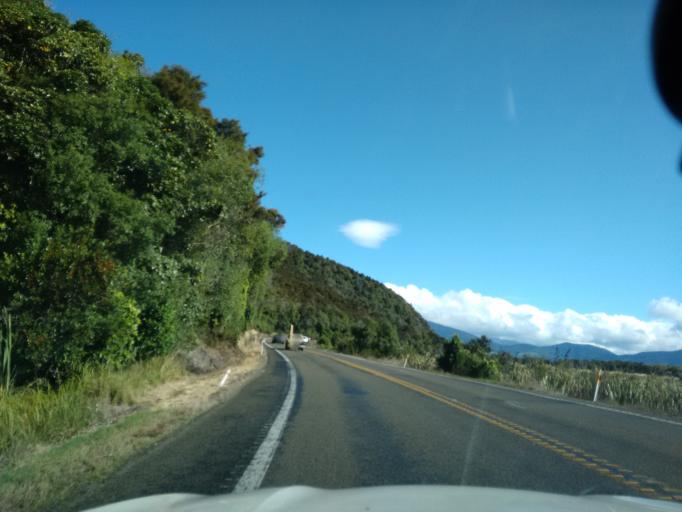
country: NZ
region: Waikato
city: Turangi
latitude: -38.9399
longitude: 175.8585
